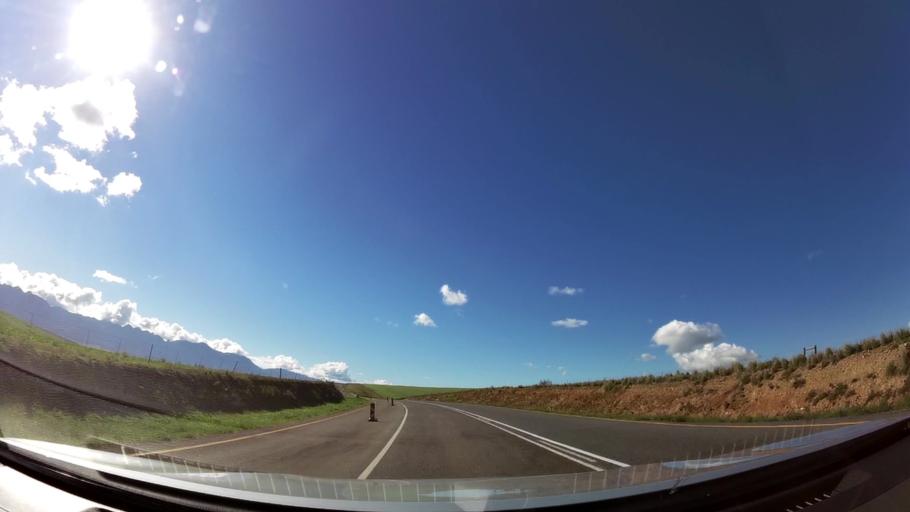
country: ZA
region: Western Cape
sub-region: Overberg District Municipality
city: Caledon
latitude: -34.1845
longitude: 19.6834
